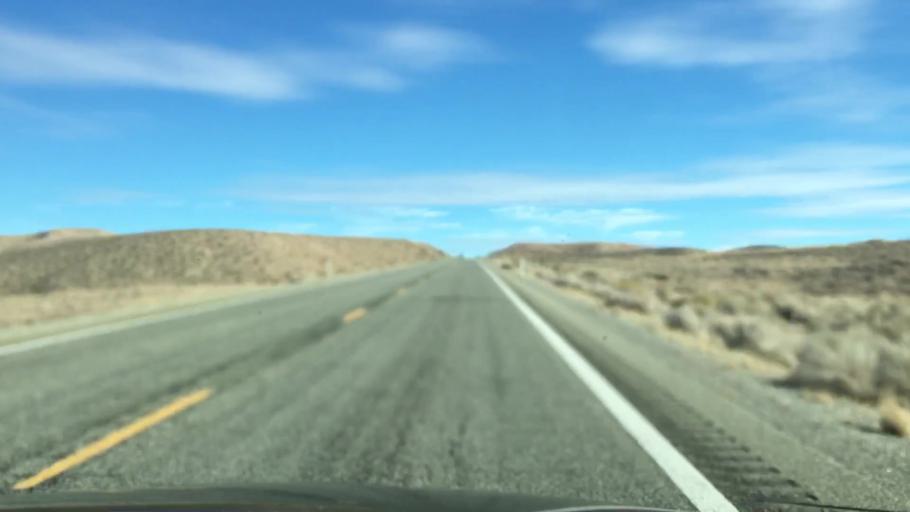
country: US
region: Nevada
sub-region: Lyon County
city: Yerington
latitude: 39.0456
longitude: -118.9643
